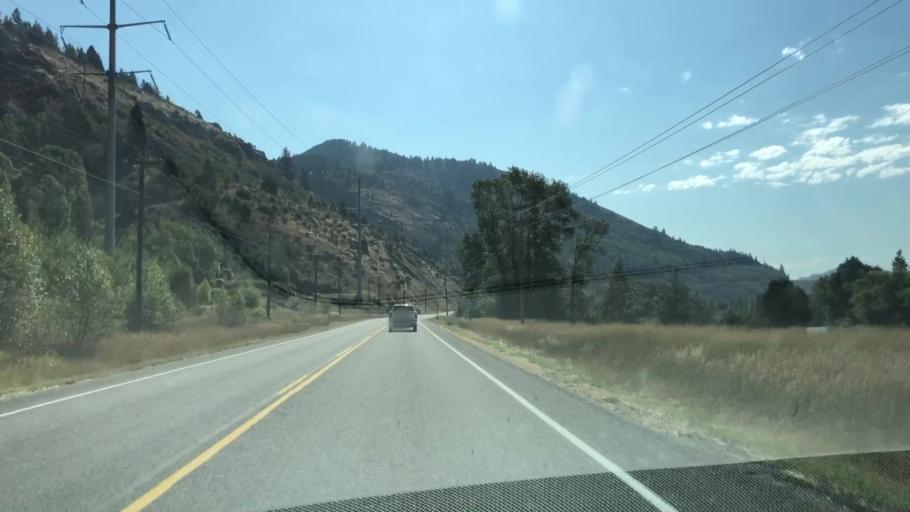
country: US
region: Idaho
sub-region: Teton County
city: Victor
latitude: 43.3476
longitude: -111.2116
